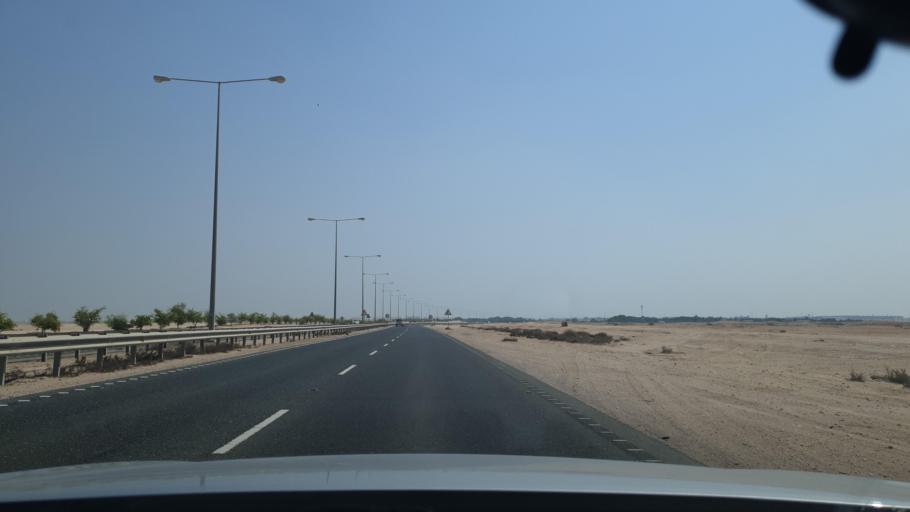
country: QA
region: Al Khawr
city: Al Khawr
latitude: 25.7400
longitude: 51.4874
